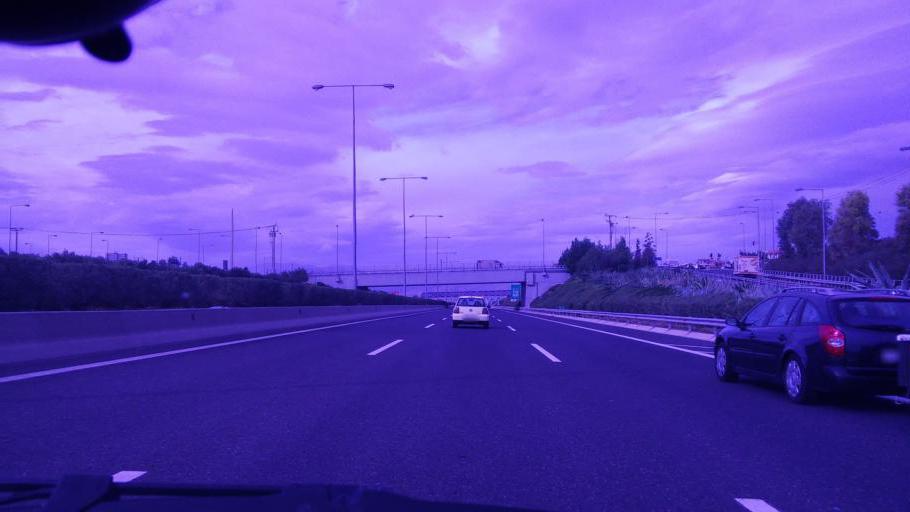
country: GR
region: Attica
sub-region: Nomarchia Dytikis Attikis
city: Aspropyrgos
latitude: 38.0896
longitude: 23.6230
